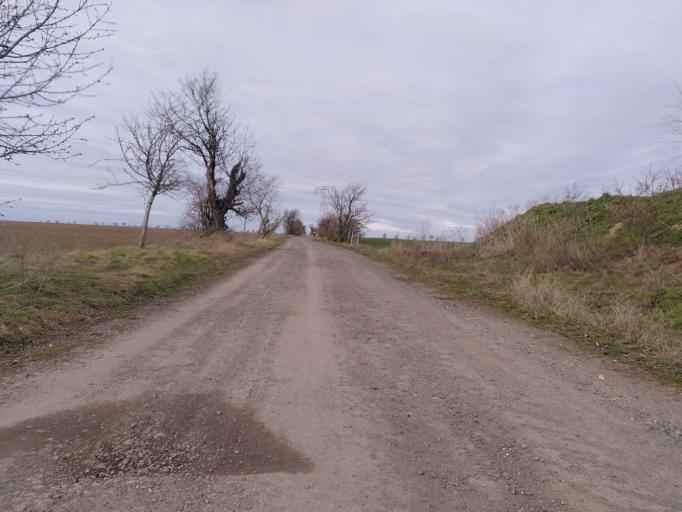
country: DE
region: Saxony-Anhalt
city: Gatersleben
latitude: 51.7921
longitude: 11.2558
